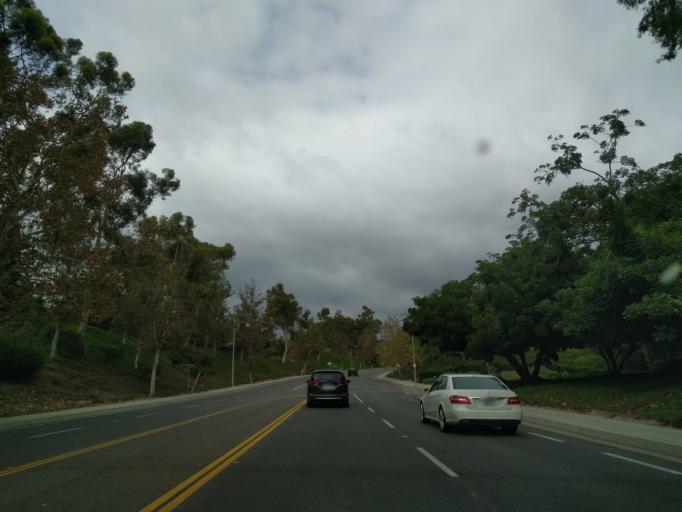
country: US
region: California
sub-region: Orange County
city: Las Flores
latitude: 33.5999
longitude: -117.6451
